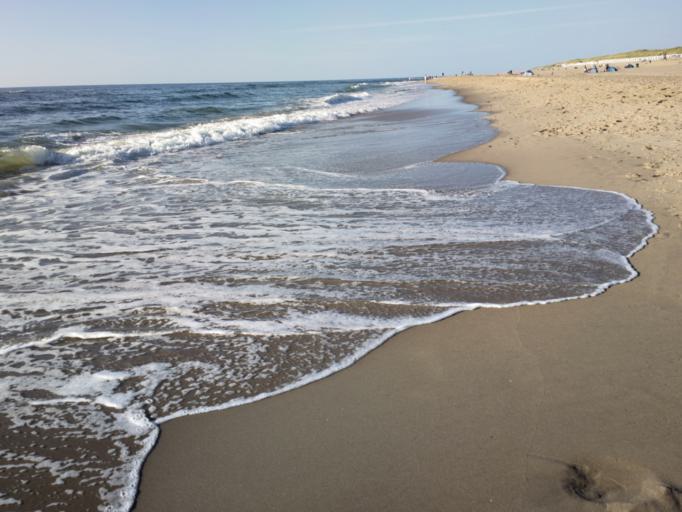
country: NL
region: North Holland
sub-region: Gemeente Texel
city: Den Burg
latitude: 53.0627
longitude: 4.7211
